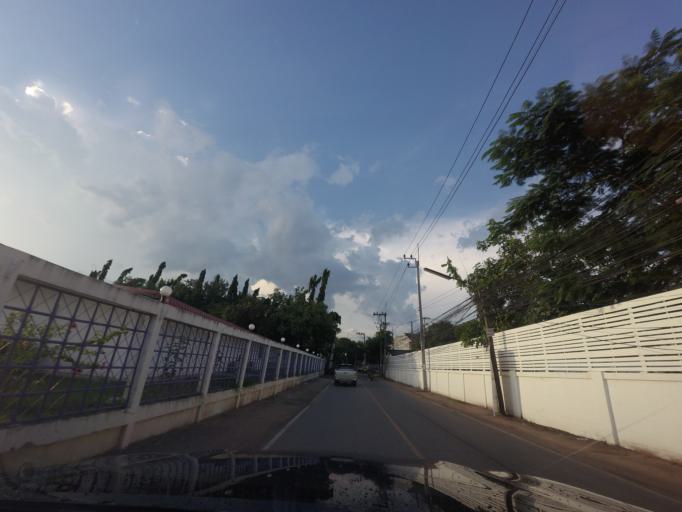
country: TH
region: Khon Kaen
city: Khon Kaen
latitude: 16.4233
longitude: 102.8627
